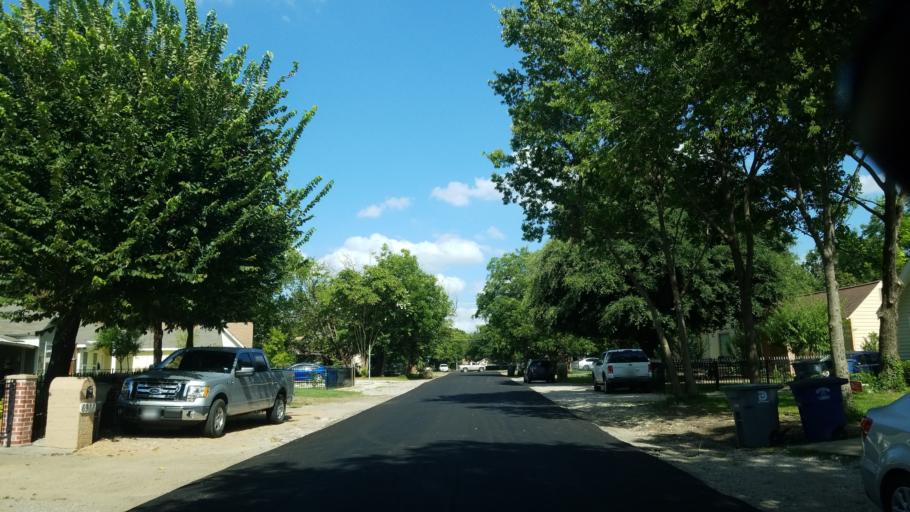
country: US
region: Texas
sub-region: Dallas County
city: Balch Springs
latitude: 32.7707
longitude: -96.7015
